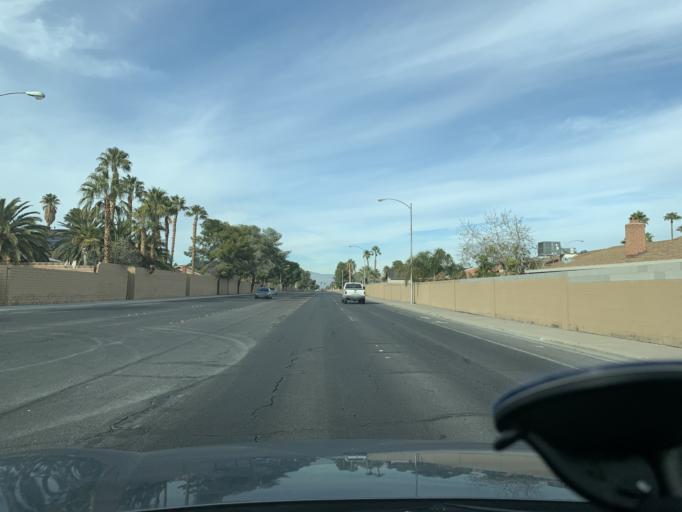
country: US
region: Nevada
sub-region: Clark County
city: Spring Valley
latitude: 36.1032
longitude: -115.2340
